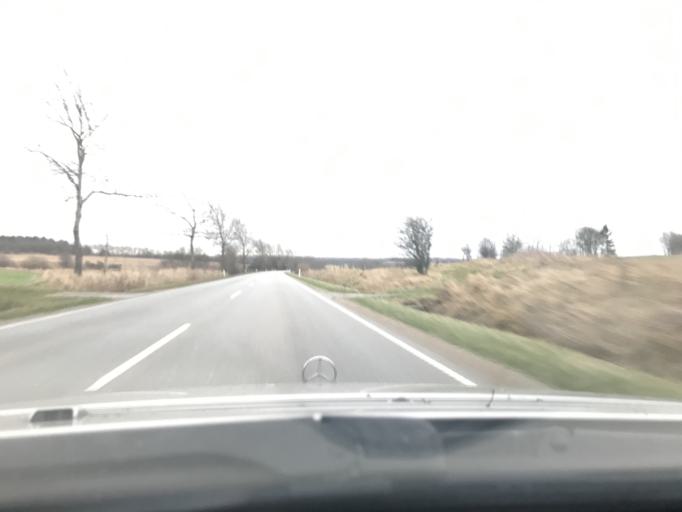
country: DK
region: South Denmark
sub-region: Aabenraa Kommune
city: Rodekro
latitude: 55.0861
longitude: 9.2127
